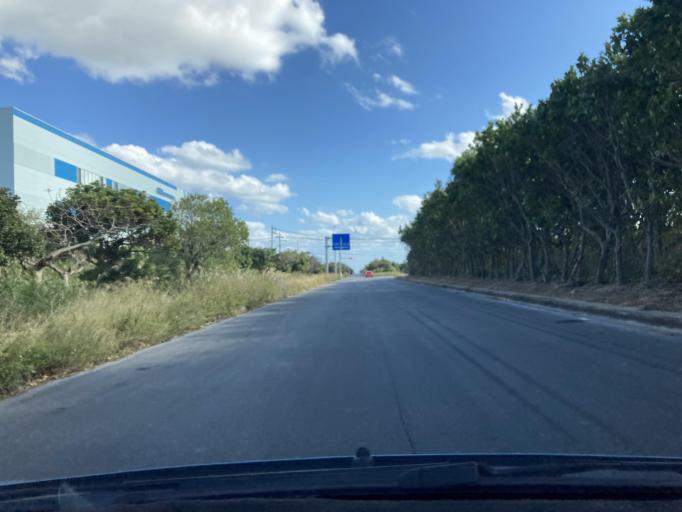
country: JP
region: Okinawa
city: Katsuren-haebaru
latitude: 26.3365
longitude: 127.8631
